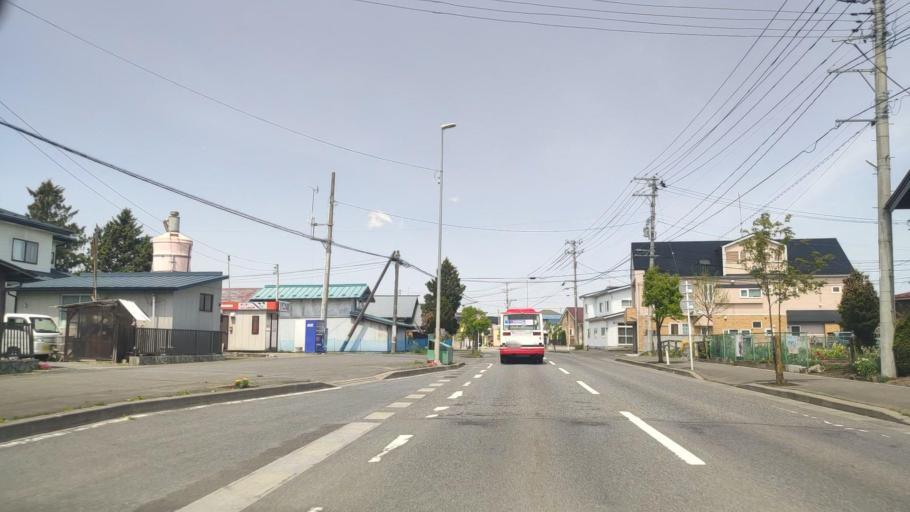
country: JP
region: Aomori
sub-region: Hachinohe Shi
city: Uchimaru
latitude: 40.5052
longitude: 141.4387
